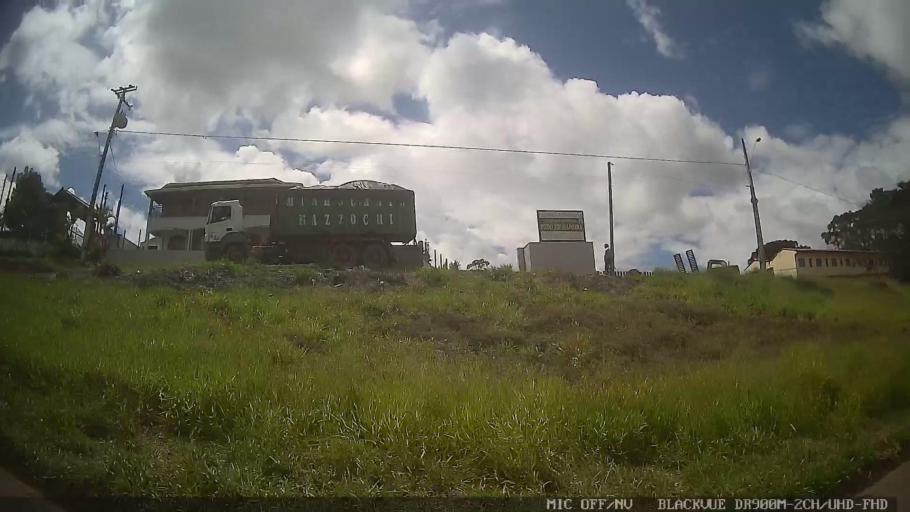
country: BR
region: Minas Gerais
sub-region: Extrema
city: Extrema
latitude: -22.8045
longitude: -46.4498
